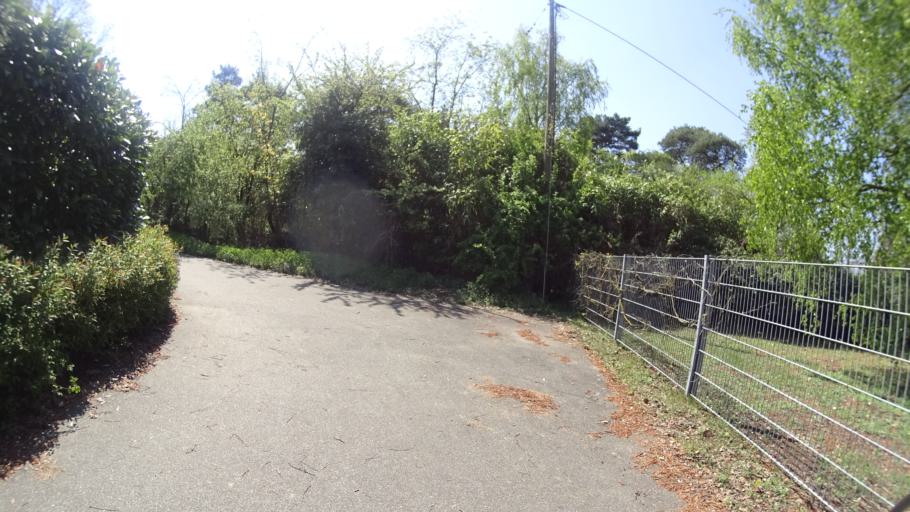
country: DE
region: Baden-Wuerttemberg
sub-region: Karlsruhe Region
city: Karlsruhe
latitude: 49.0400
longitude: 8.3929
